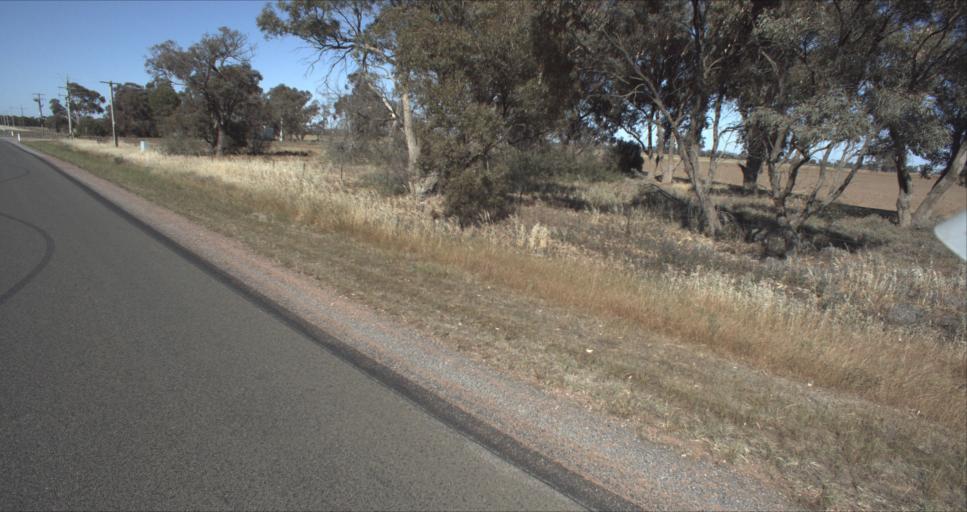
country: AU
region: New South Wales
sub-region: Leeton
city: Leeton
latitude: -34.5764
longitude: 146.2625
